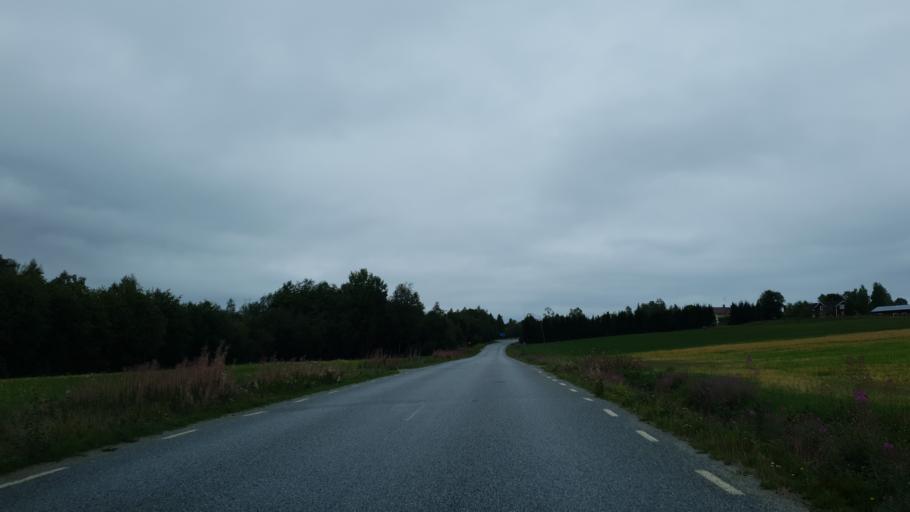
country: SE
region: Vaesterbotten
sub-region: Skelleftea Kommun
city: Burea
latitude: 64.3993
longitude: 21.2908
